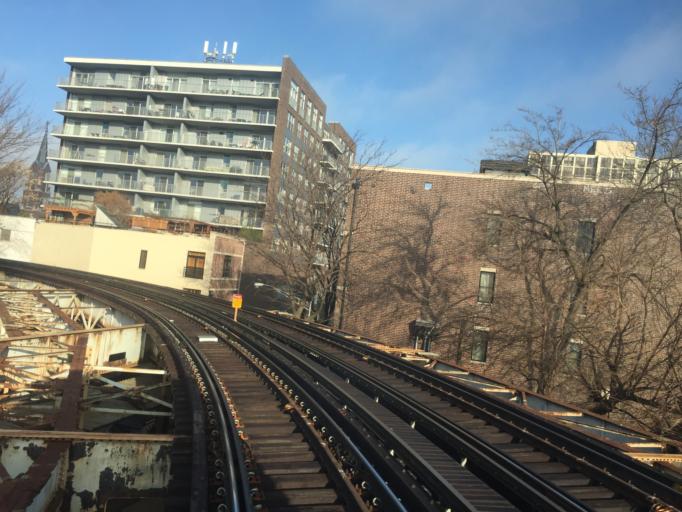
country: US
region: Illinois
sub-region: Cook County
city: Chicago
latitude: 41.9100
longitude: -87.6374
